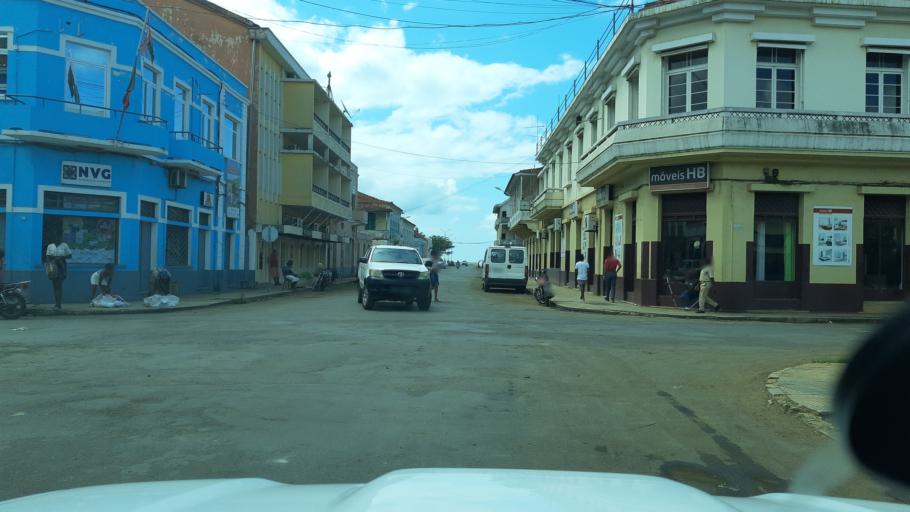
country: ST
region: Sao Tome Island
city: Sao Tome
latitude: 0.3375
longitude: 6.7308
